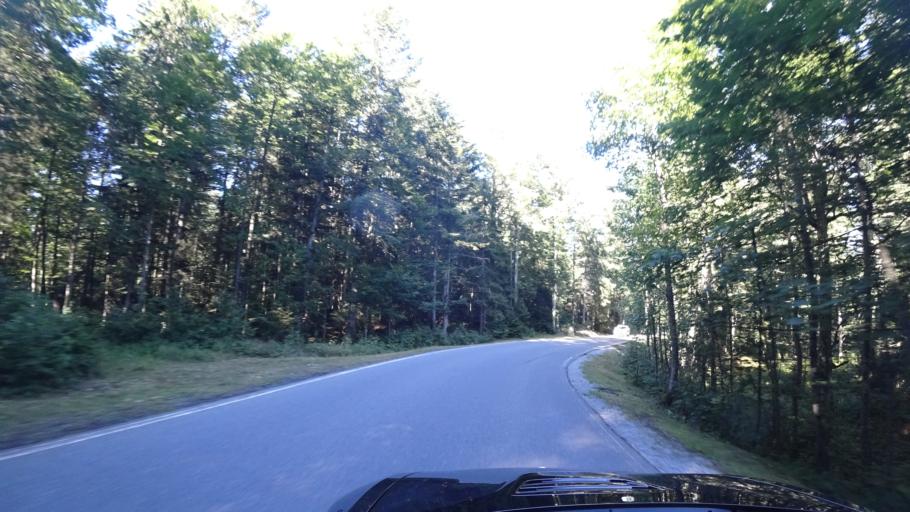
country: CH
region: Obwalden
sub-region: Obwalden
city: Lungern
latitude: 46.8273
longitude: 8.1157
